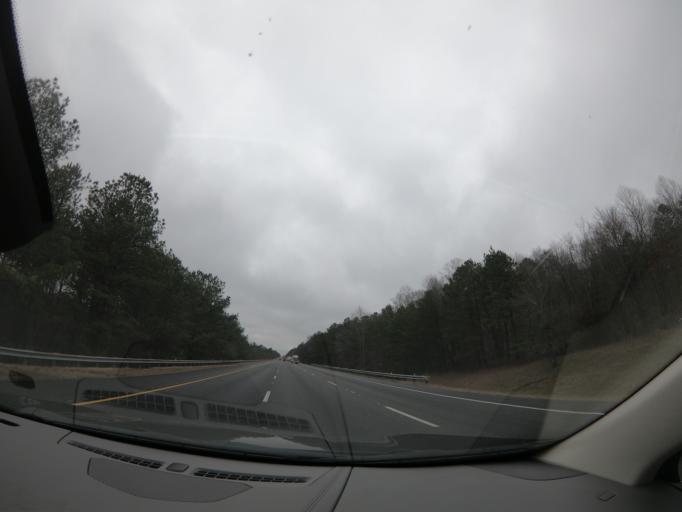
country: US
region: Georgia
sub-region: Whitfield County
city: Dalton
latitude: 34.8283
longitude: -85.0171
